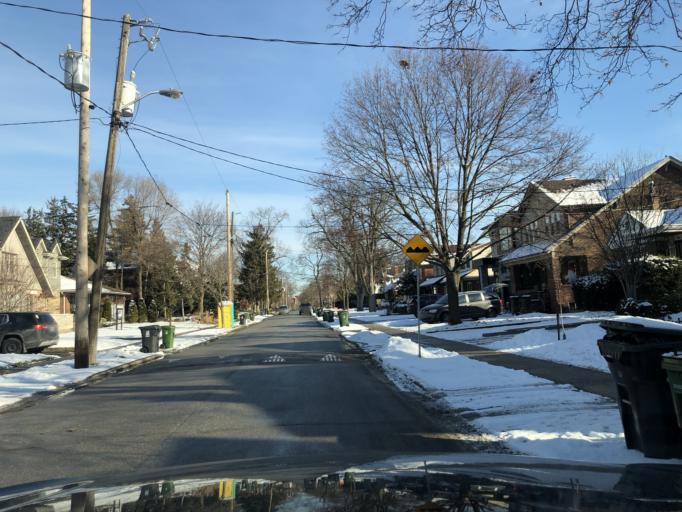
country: CA
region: Ontario
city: Etobicoke
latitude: 43.7062
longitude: -79.5153
